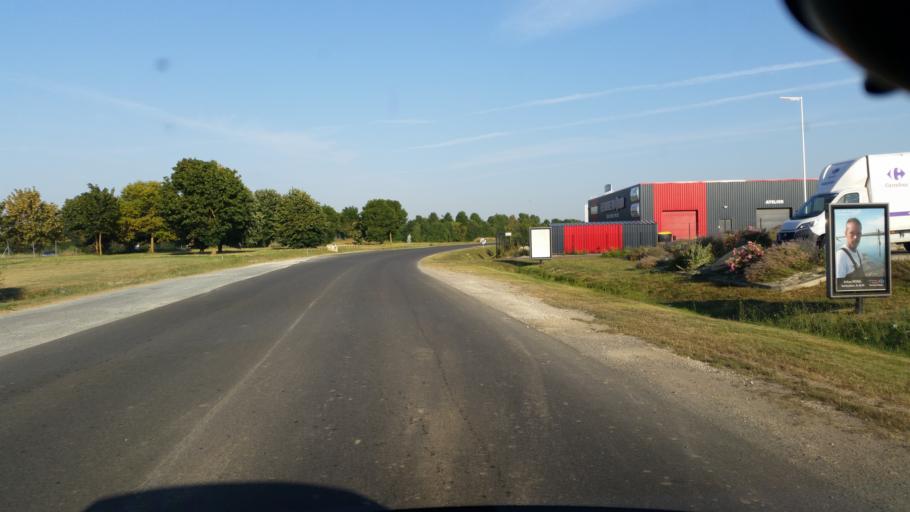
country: FR
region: Poitou-Charentes
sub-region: Departement de la Charente-Maritime
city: Saint-Jean-de-Liversay
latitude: 46.2270
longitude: -0.8734
